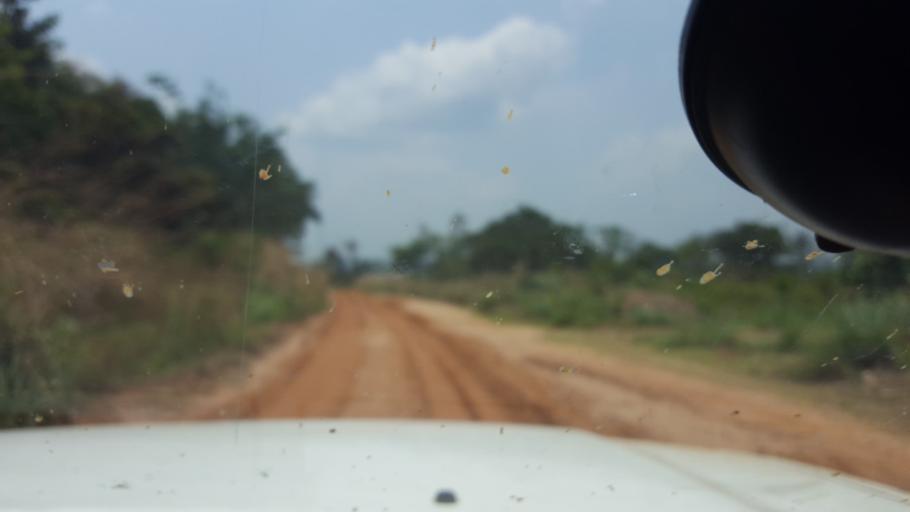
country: CD
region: Bandundu
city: Mushie
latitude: -3.7504
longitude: 16.6344
